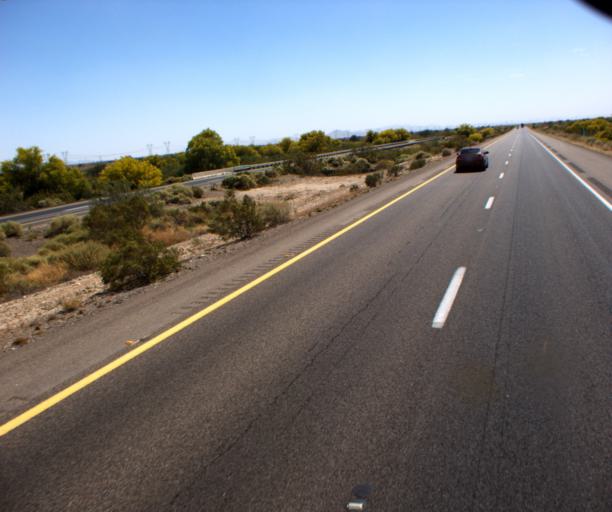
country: US
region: Arizona
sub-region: Maricopa County
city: Gila Bend
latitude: 33.0758
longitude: -112.6468
